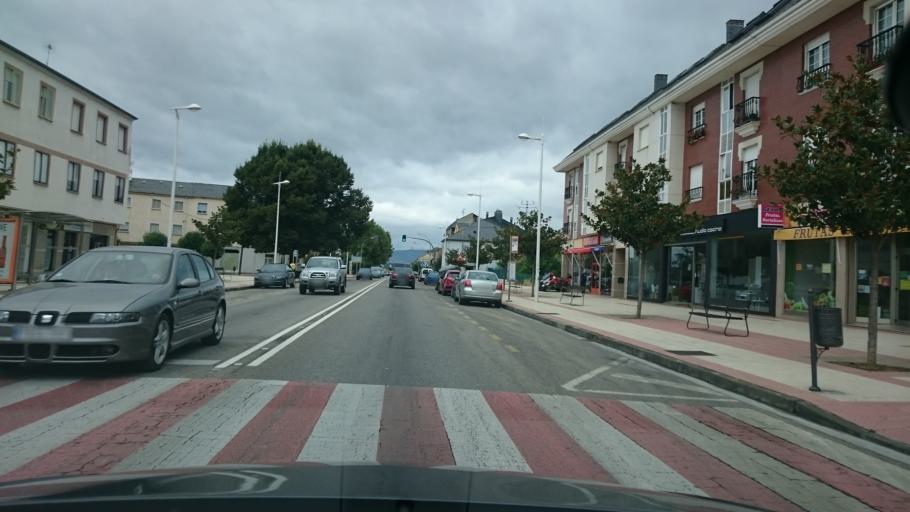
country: ES
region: Castille and Leon
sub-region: Provincia de Leon
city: Ponferrada
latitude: 42.5617
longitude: -6.6284
